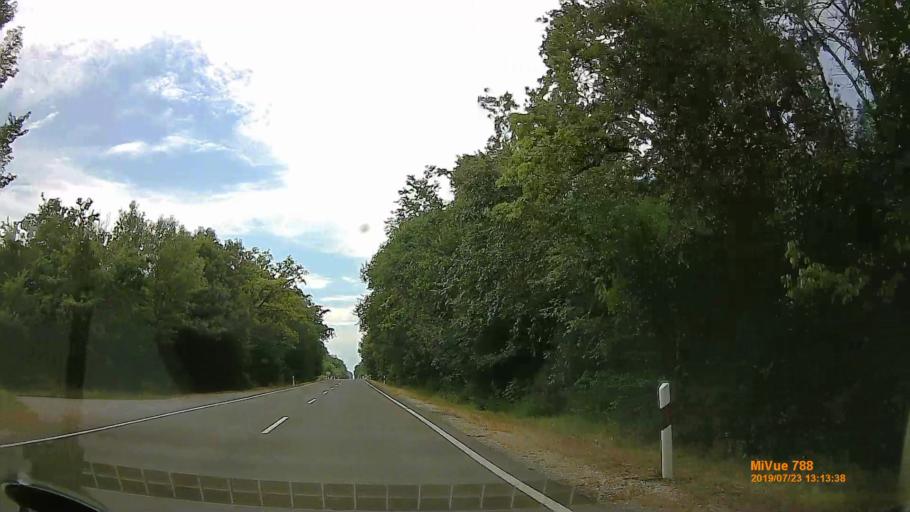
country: HU
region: Hajdu-Bihar
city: Gorbehaza
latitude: 47.9238
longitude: 21.2269
